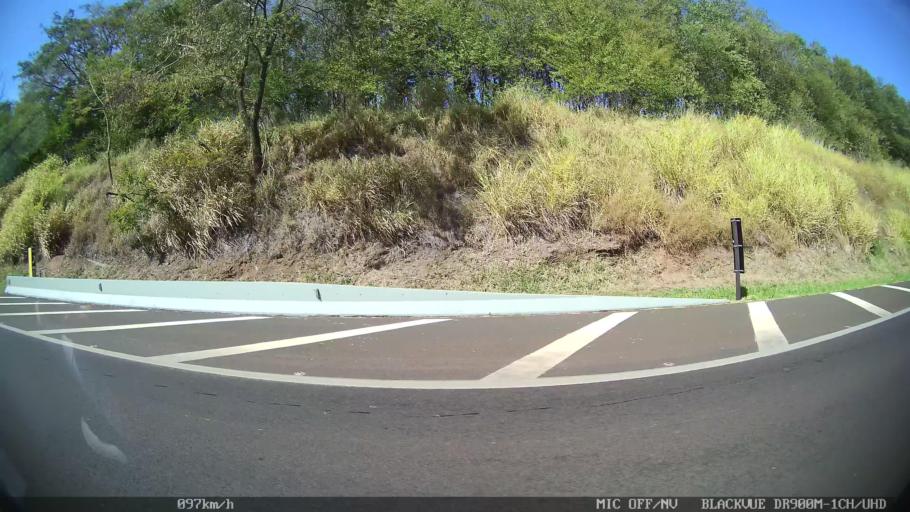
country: BR
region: Sao Paulo
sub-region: Franca
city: Franca
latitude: -20.5855
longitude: -47.4336
